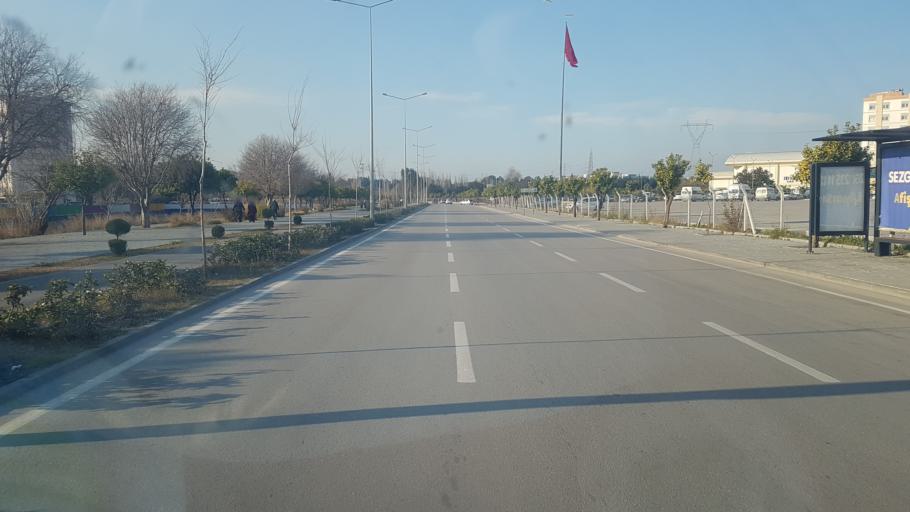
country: TR
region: Adana
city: Adana
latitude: 37.0090
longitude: 35.3536
